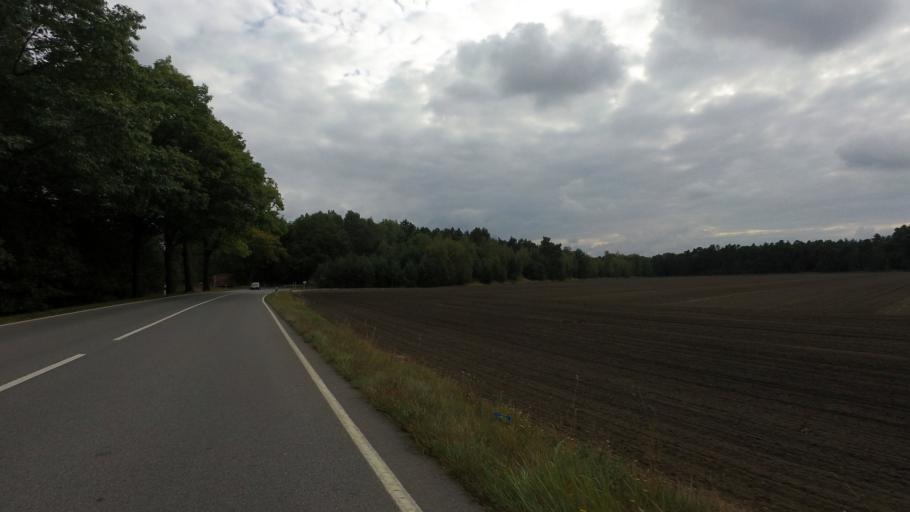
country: DE
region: Saxony
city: Wittichenau
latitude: 51.3926
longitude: 14.2967
